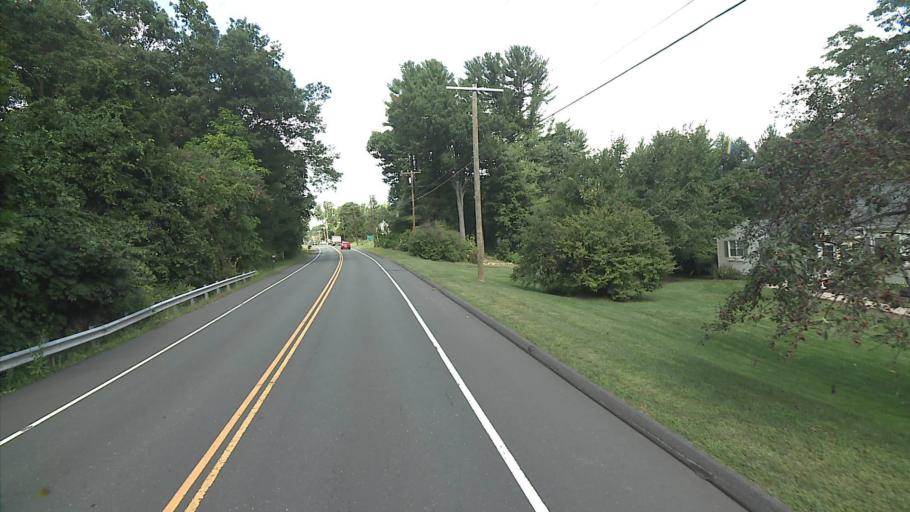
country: US
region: Connecticut
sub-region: Hartford County
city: Salmon Brook
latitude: 41.9470
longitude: -72.7805
